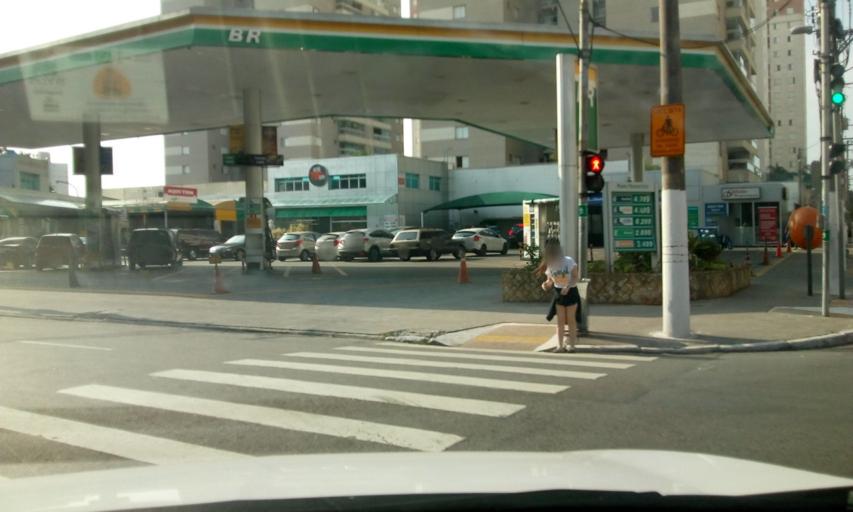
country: BR
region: Sao Paulo
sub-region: Sao Paulo
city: Sao Paulo
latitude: -23.5497
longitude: -46.5961
